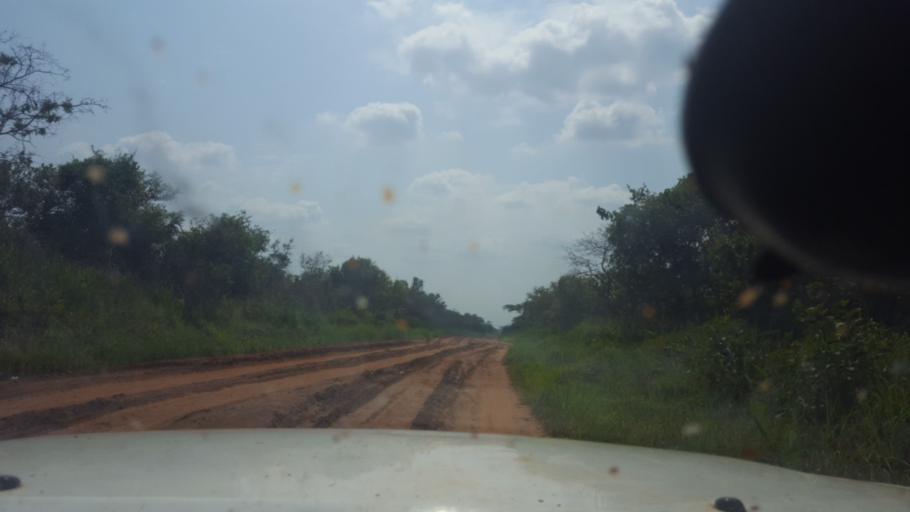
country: CD
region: Bandundu
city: Bandundu
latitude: -3.7620
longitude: 17.1482
